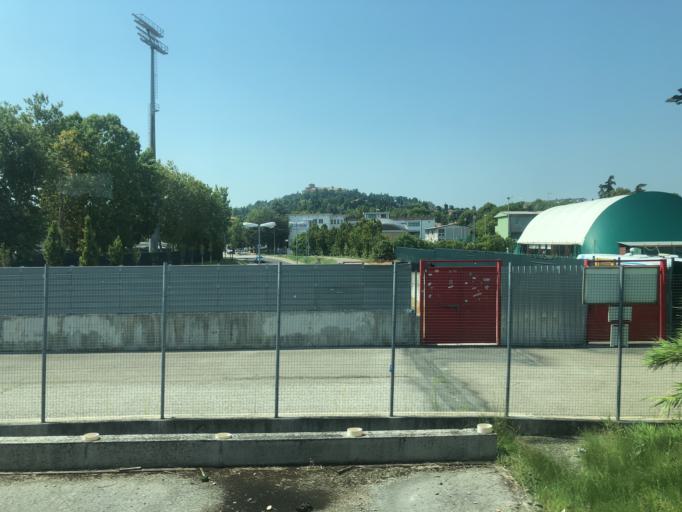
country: IT
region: Emilia-Romagna
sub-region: Forli-Cesena
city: Cesena
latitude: 44.1418
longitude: 12.2612
